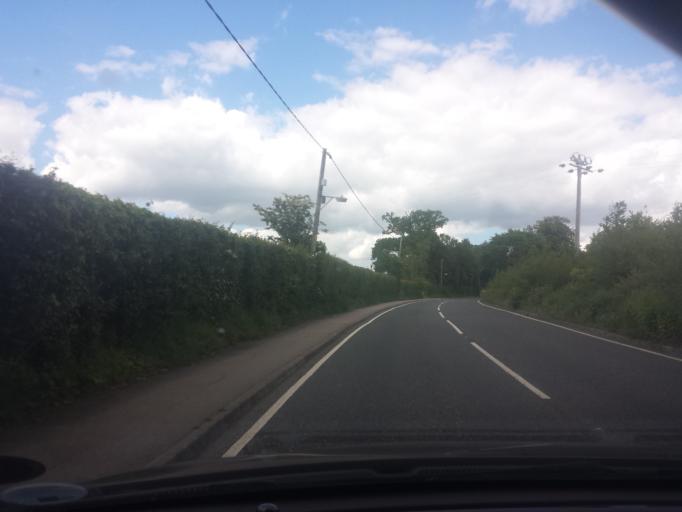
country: GB
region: England
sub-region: Essex
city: Little Clacton
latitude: 51.8496
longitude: 1.1629
